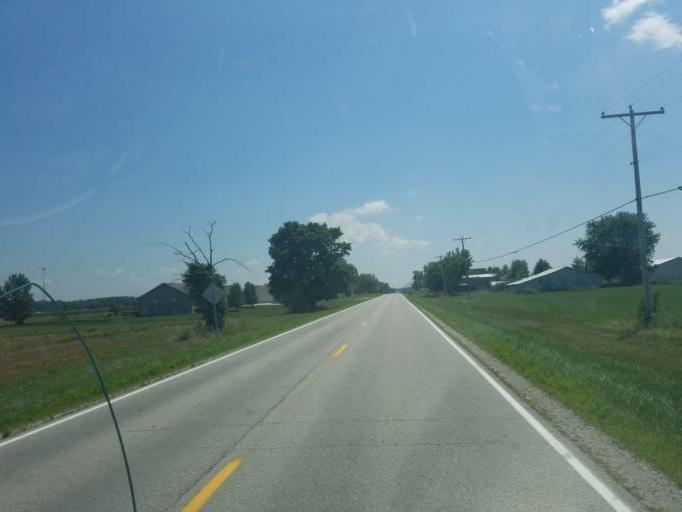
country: US
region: Ohio
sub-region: Shelby County
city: Anna
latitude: 40.4231
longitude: -84.1766
